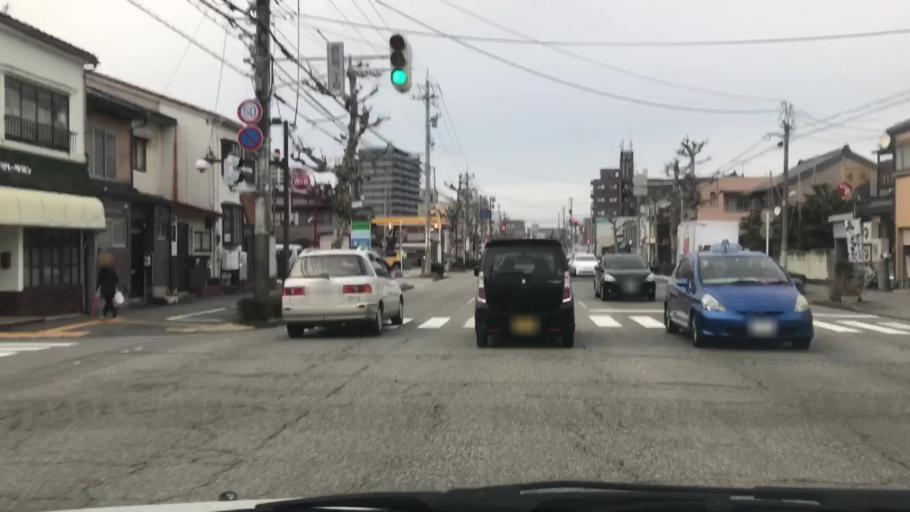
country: JP
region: Toyama
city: Toyama-shi
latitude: 36.6850
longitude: 137.2221
